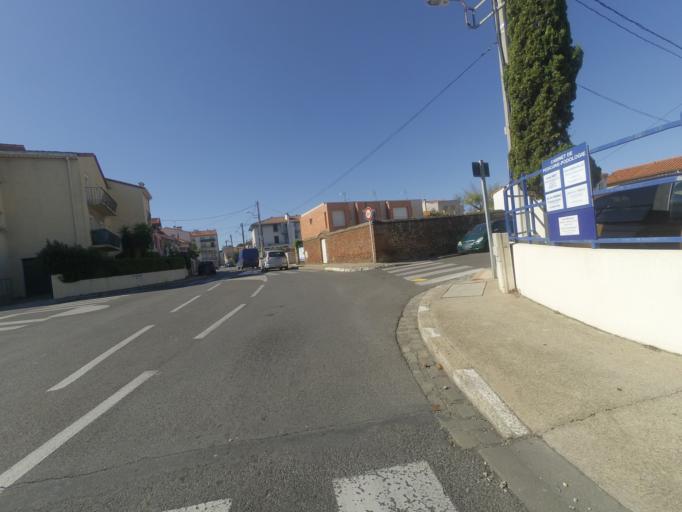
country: FR
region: Languedoc-Roussillon
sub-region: Departement des Pyrenees-Orientales
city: Perpignan
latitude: 42.6906
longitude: 2.9122
